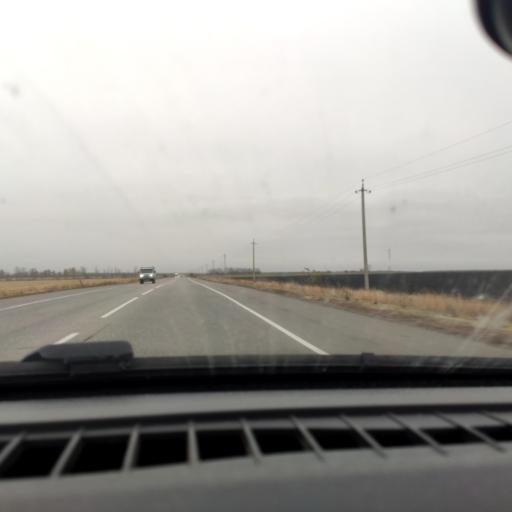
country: RU
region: Voronezj
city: Strelitsa
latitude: 51.5548
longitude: 38.9726
